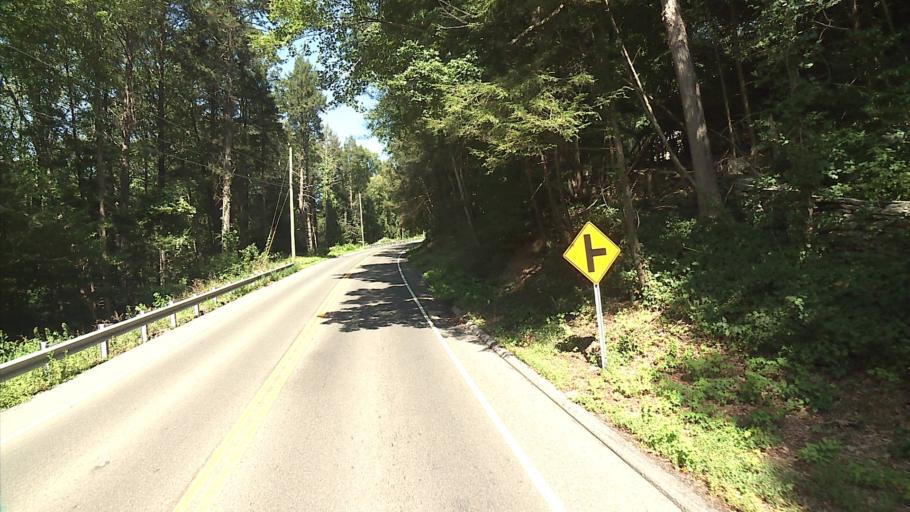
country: US
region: Connecticut
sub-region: New Haven County
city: Ansonia
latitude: 41.3672
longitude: -73.1365
